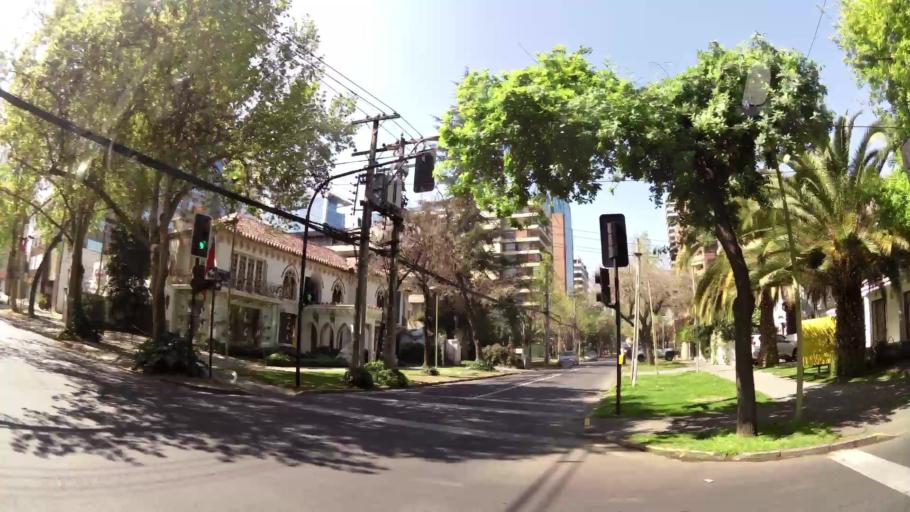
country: CL
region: Santiago Metropolitan
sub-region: Provincia de Santiago
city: Villa Presidente Frei, Nunoa, Santiago, Chile
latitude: -33.4173
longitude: -70.5937
